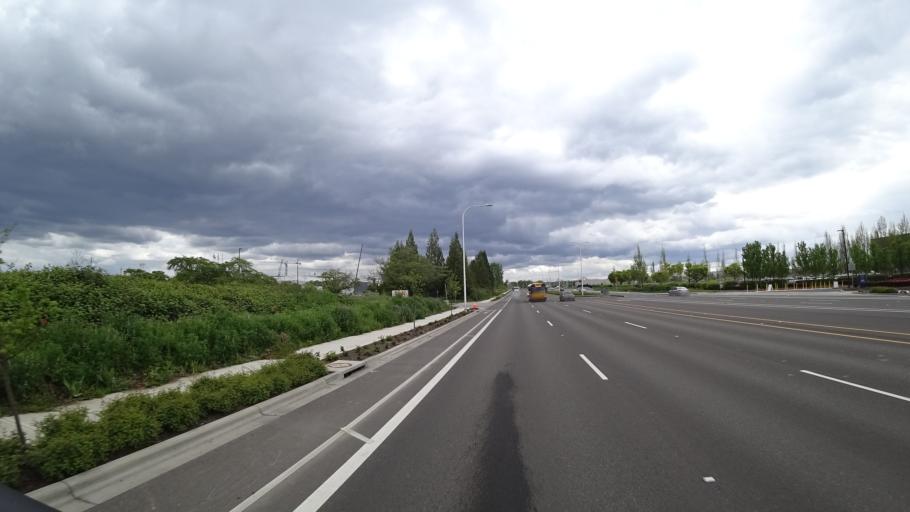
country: US
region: Oregon
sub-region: Washington County
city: Rockcreek
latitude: 45.5540
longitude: -122.9262
